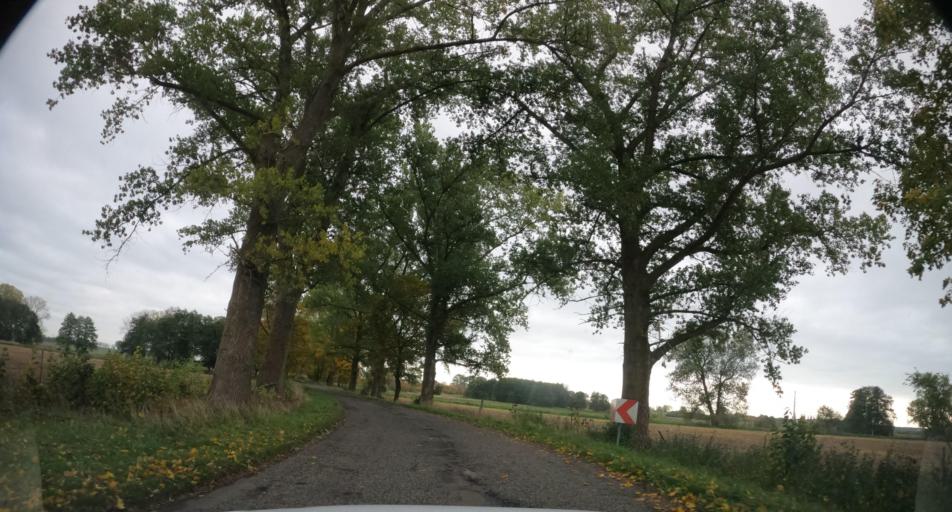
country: PL
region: West Pomeranian Voivodeship
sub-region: Powiat kamienski
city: Wolin
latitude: 53.8605
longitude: 14.5971
